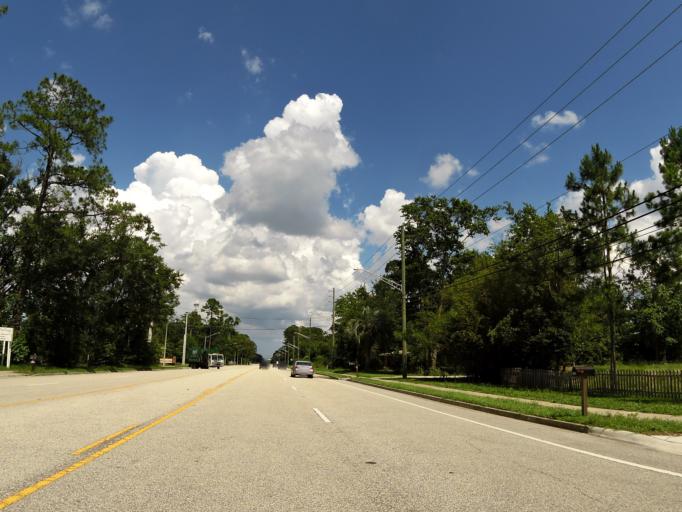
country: US
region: Florida
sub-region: Saint Johns County
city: Fruit Cove
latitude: 30.1473
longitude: -81.5701
